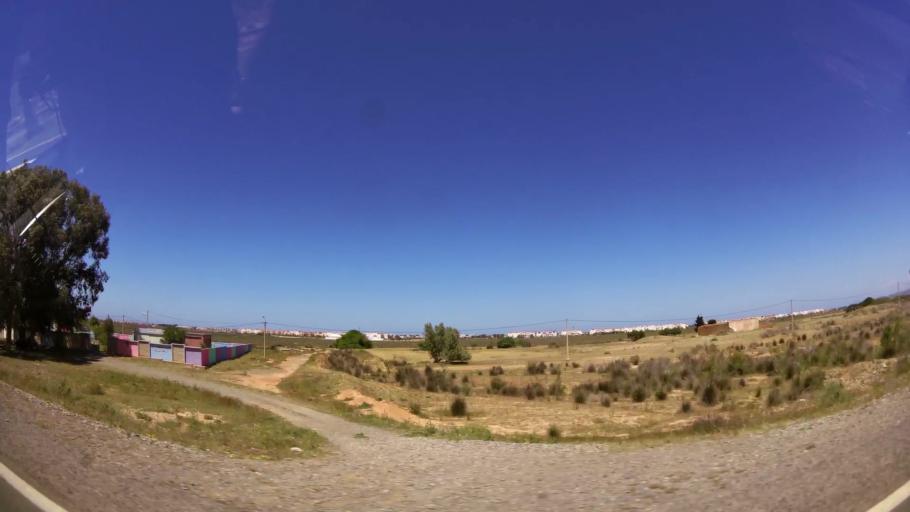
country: MA
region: Oriental
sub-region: Berkane-Taourirt
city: Madagh
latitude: 35.0952
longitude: -2.3164
